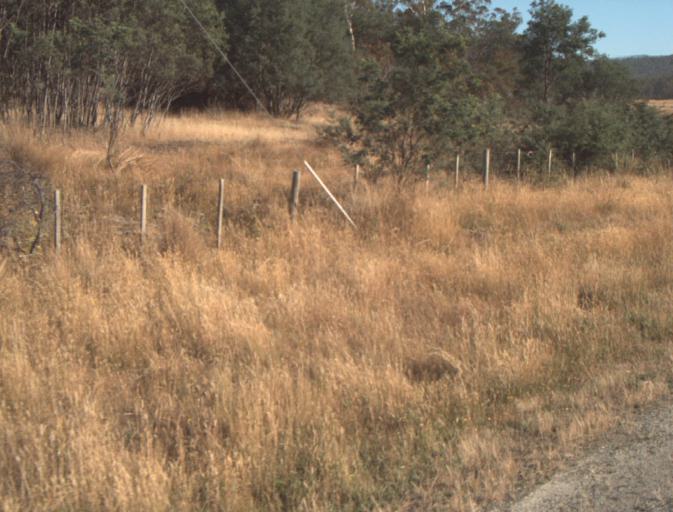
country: AU
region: Tasmania
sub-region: Launceston
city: Newstead
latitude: -41.4423
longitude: 147.2540
